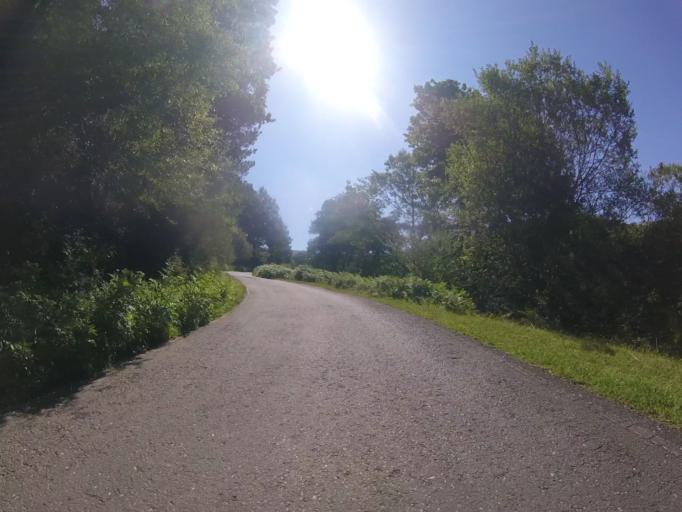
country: ES
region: Navarre
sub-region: Provincia de Navarra
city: Goizueta
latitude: 43.1869
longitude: -1.8381
